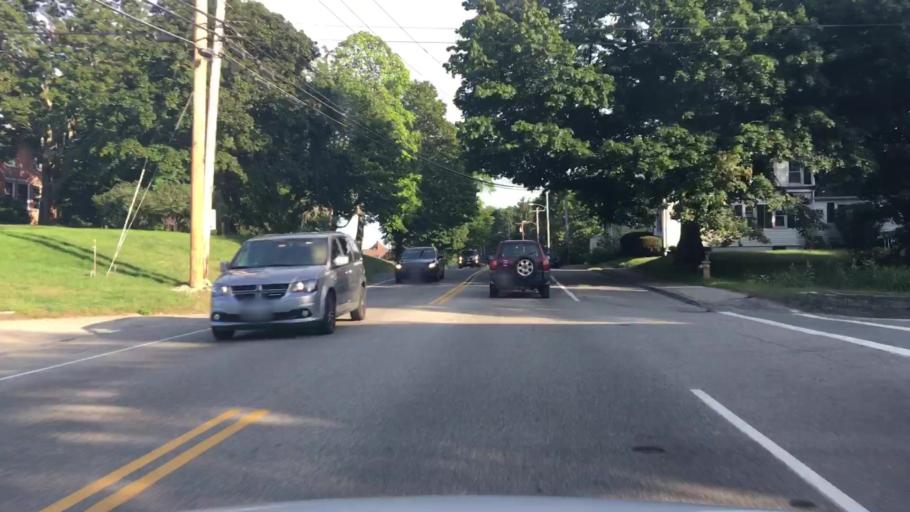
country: US
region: Maine
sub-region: Cumberland County
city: Westbrook
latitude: 43.6854
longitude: -70.3564
